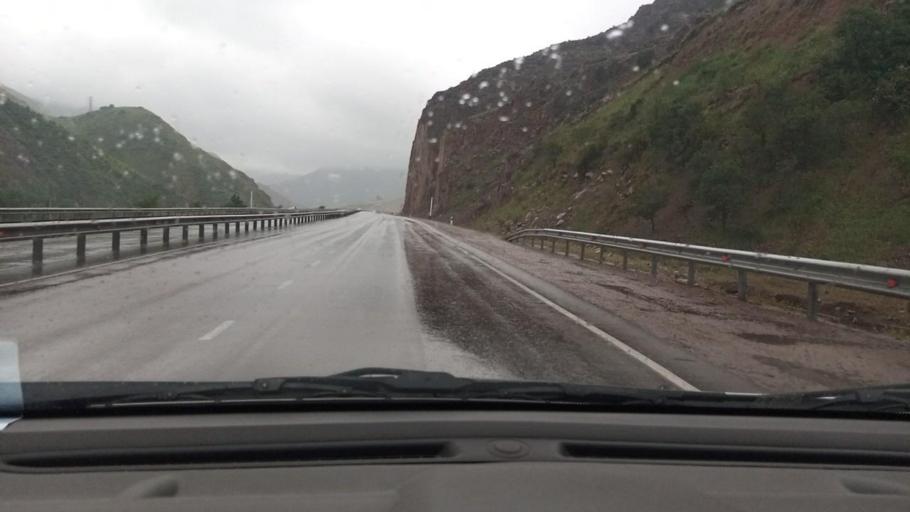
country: UZ
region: Toshkent
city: Angren
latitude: 41.1214
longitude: 70.3500
